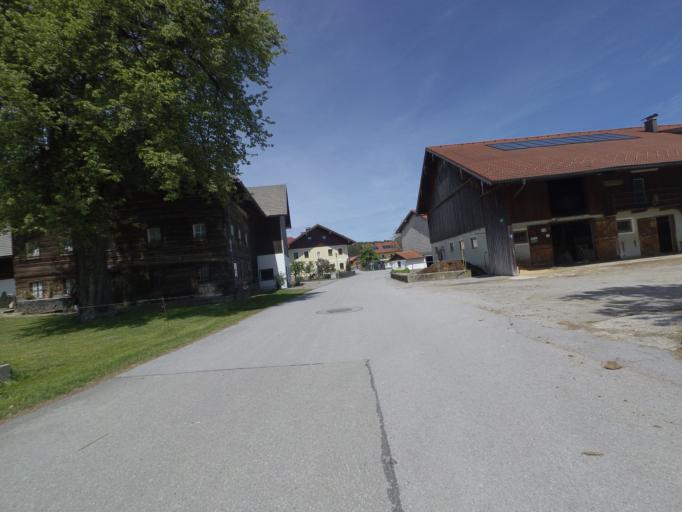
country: AT
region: Salzburg
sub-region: Politischer Bezirk Salzburg-Umgebung
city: Berndorf bei Salzburg
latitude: 47.9820
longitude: 13.0810
